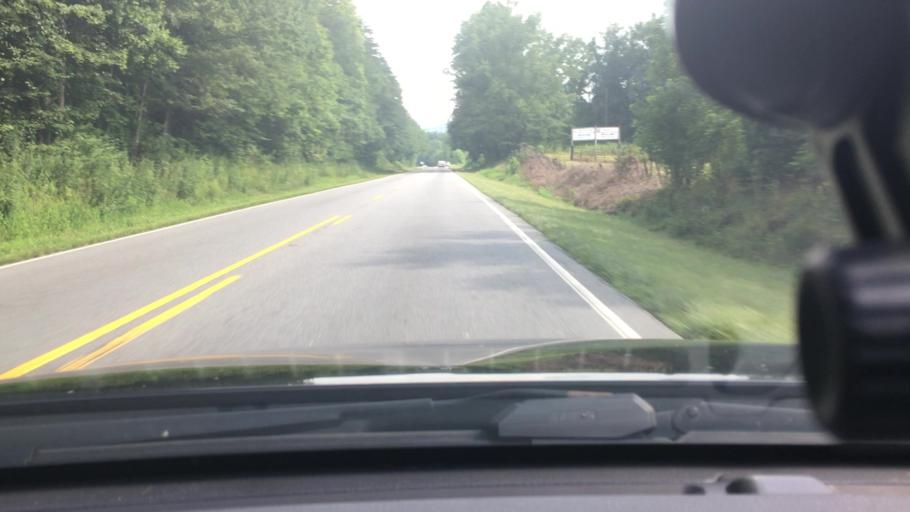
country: US
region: North Carolina
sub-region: McDowell County
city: West Marion
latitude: 35.5932
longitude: -81.9836
